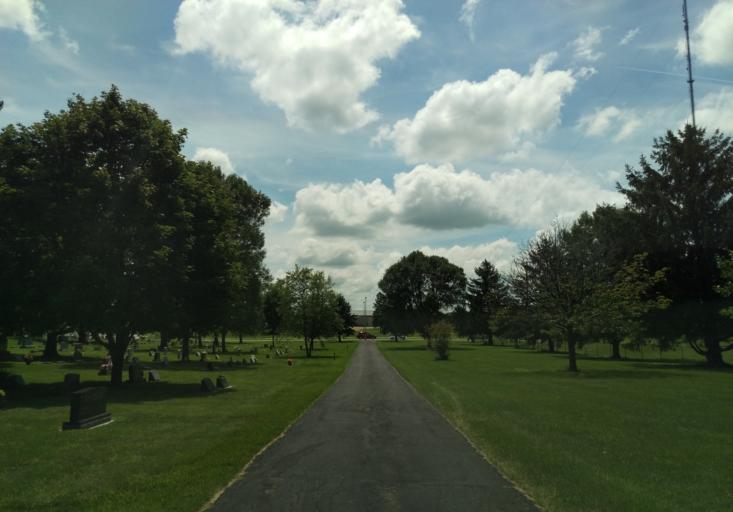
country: US
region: Wisconsin
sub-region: Dane County
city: Middleton
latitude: 43.0617
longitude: -89.5302
